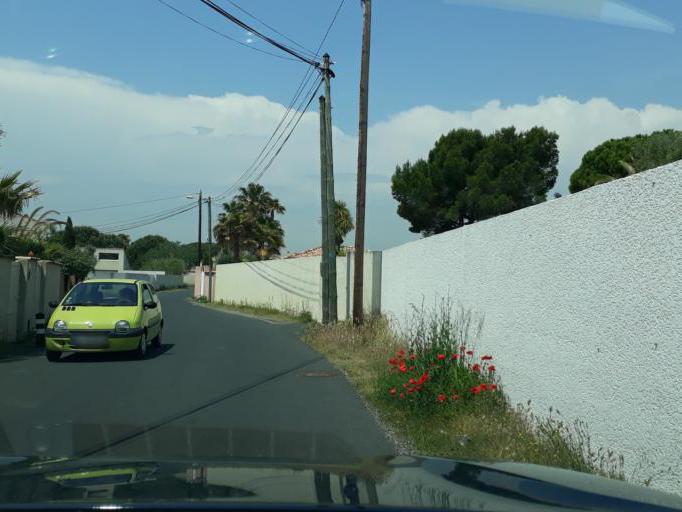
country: FR
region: Languedoc-Roussillon
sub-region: Departement de l'Herault
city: Agde
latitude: 43.2855
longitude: 3.4673
